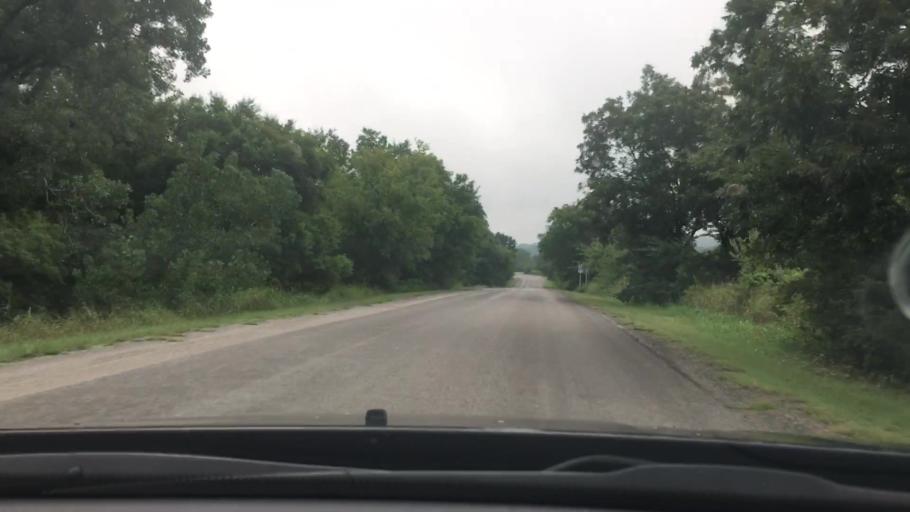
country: US
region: Oklahoma
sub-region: Murray County
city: Davis
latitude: 34.4552
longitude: -97.1377
